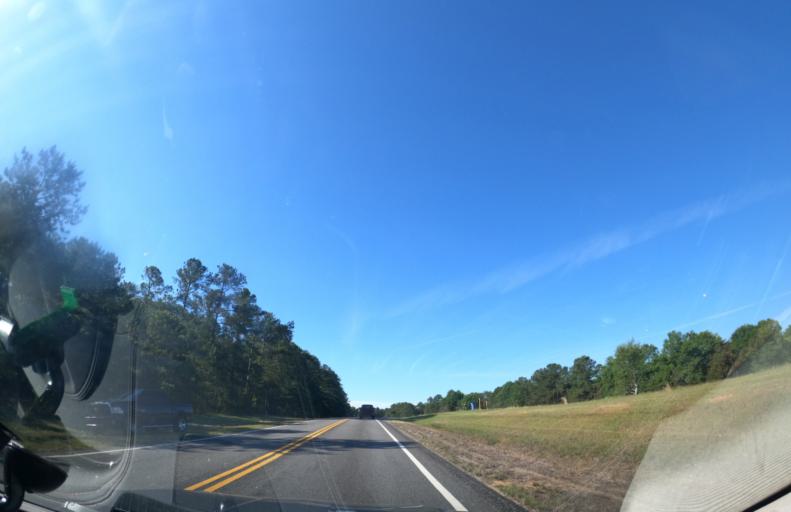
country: US
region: Georgia
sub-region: Columbia County
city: Harlem
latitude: 33.3590
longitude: -82.3253
